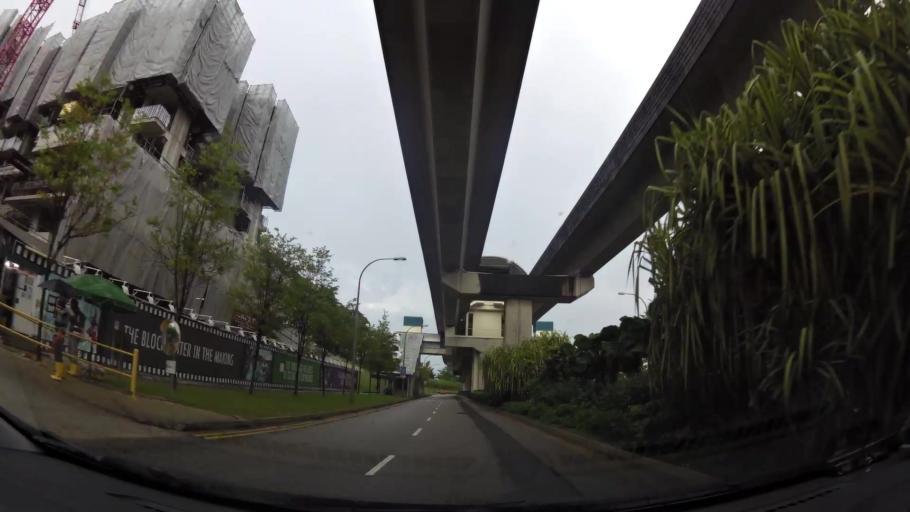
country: MY
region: Johor
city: Kampung Pasir Gudang Baru
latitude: 1.3966
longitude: 103.8755
